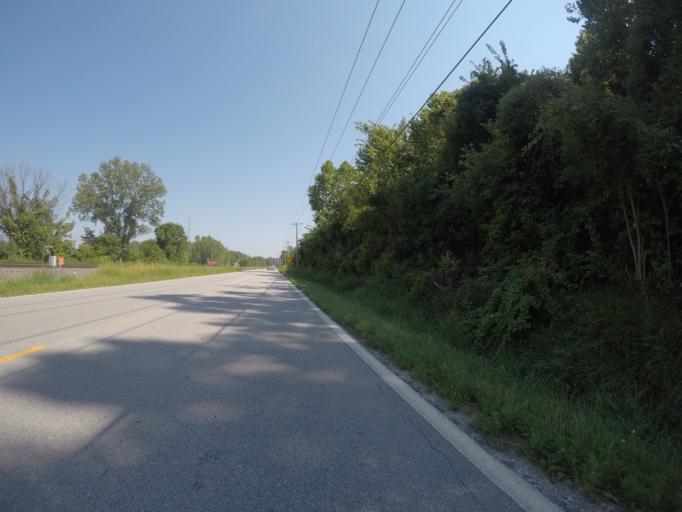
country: US
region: Kansas
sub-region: Leavenworth County
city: Lansing
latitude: 39.1921
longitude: -94.8061
